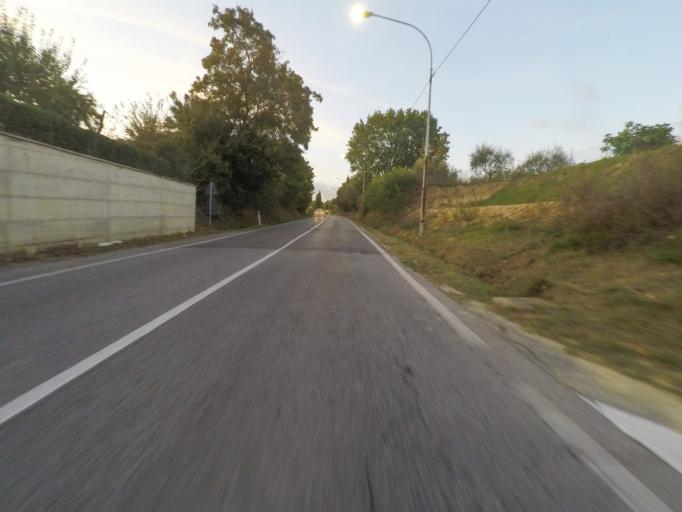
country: IT
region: Tuscany
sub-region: Provincia di Siena
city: Torrita di Siena
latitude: 43.1735
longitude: 11.7739
